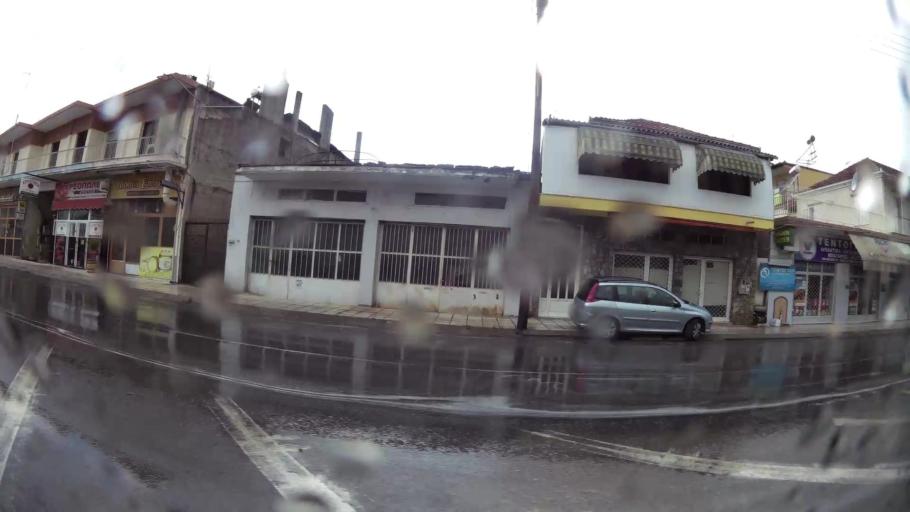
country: GR
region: Central Macedonia
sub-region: Nomos Imathias
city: Veroia
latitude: 40.5374
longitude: 22.2024
